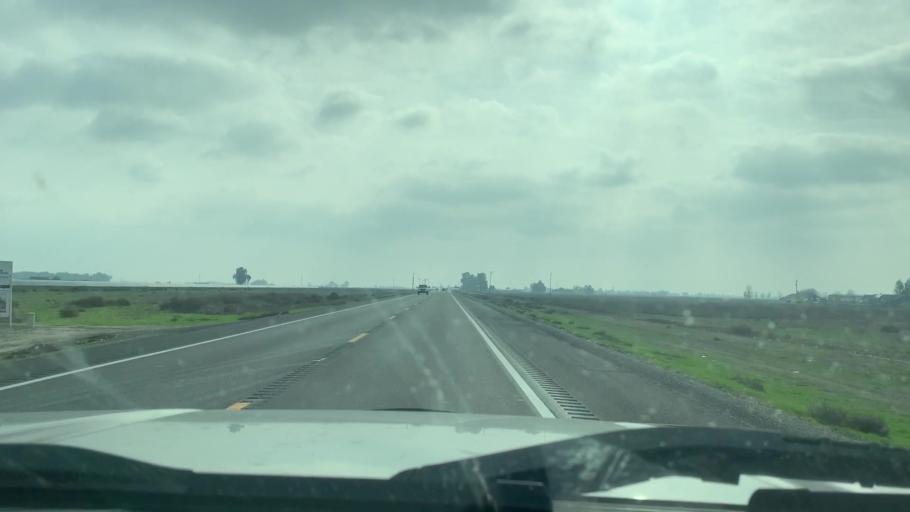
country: US
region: California
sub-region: Kings County
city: Stratford
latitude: 36.2190
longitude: -119.8162
